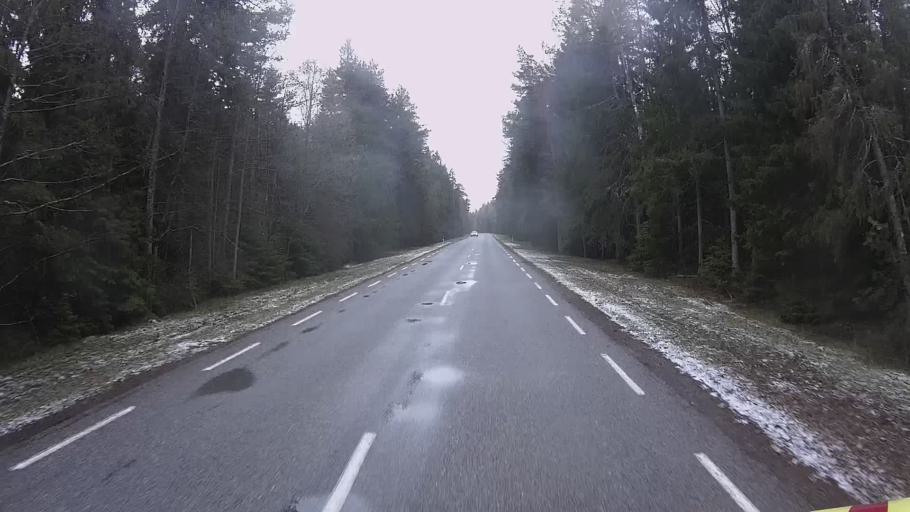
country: EE
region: Hiiumaa
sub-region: Kaerdla linn
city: Kardla
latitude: 59.0573
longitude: 22.6830
